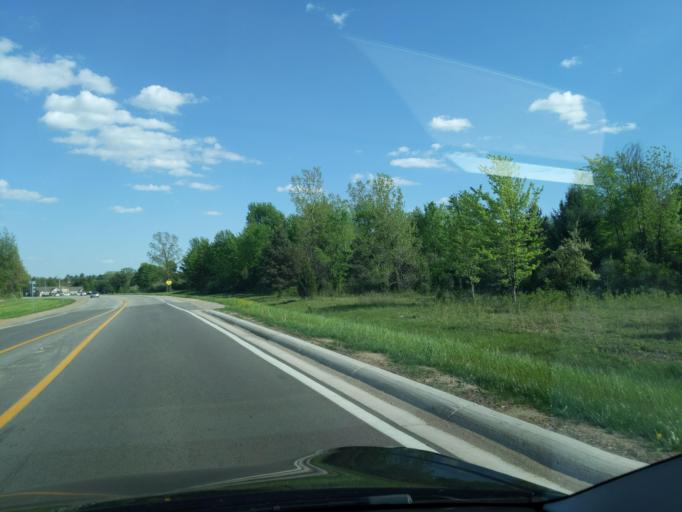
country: US
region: Michigan
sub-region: Eaton County
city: Grand Ledge
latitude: 42.7432
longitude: -84.7588
